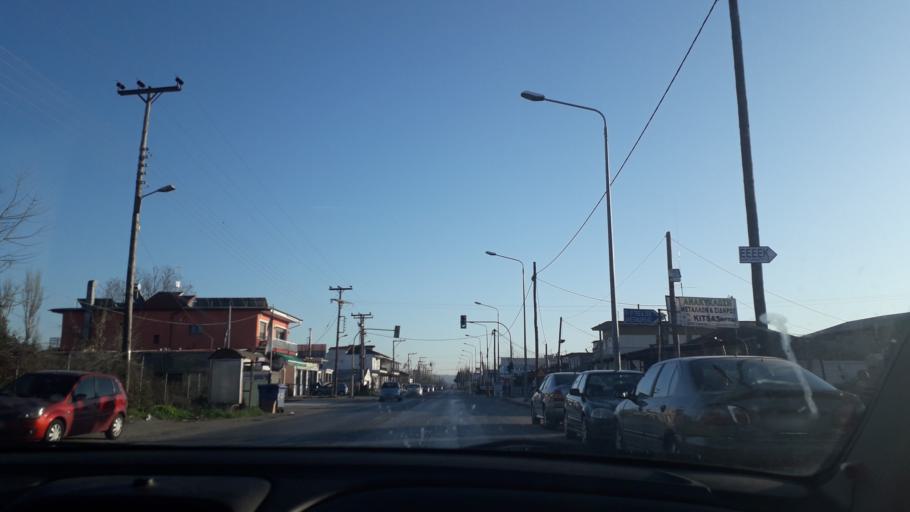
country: GR
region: Central Macedonia
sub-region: Nomos Imathias
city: Alexandreia
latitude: 40.6199
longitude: 22.4475
